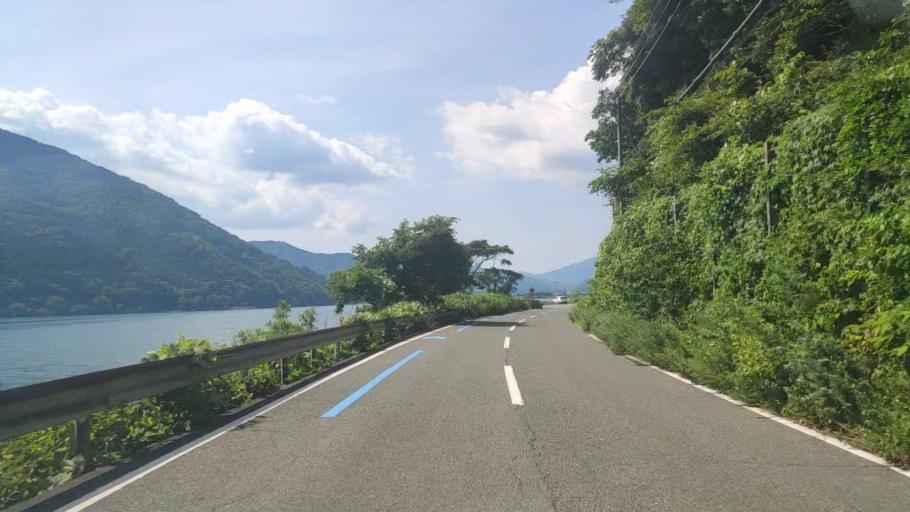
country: JP
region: Shiga Prefecture
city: Nagahama
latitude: 35.5025
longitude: 136.1702
